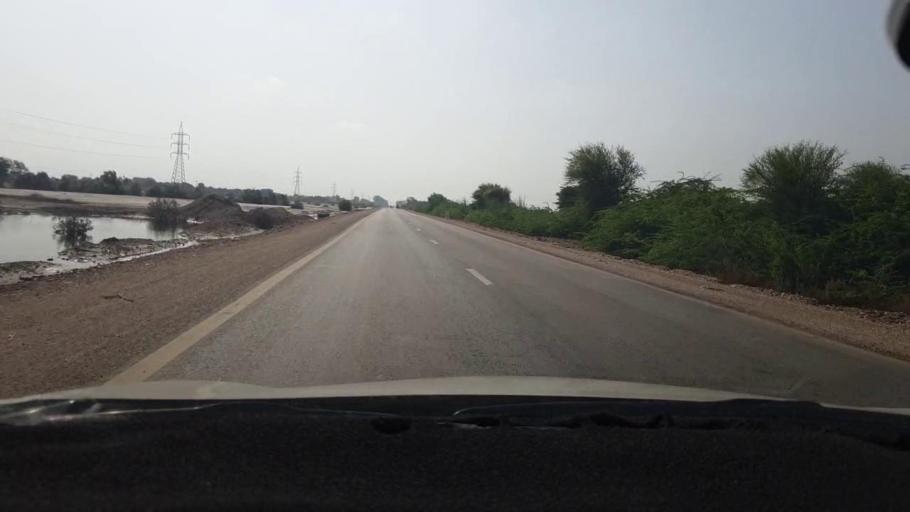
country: PK
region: Sindh
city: Jhol
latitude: 25.9108
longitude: 69.0134
